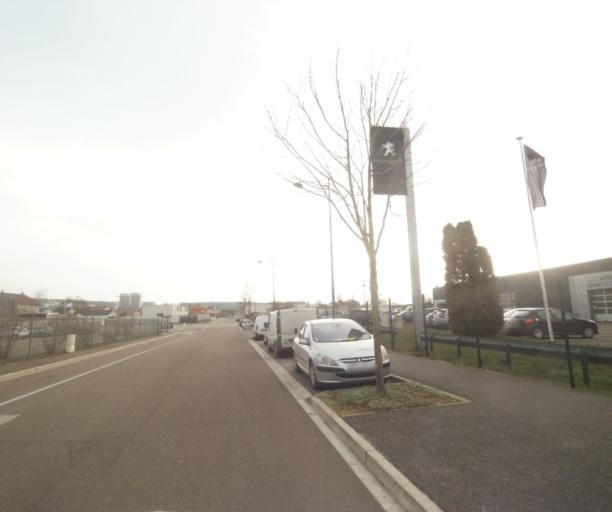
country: FR
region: Champagne-Ardenne
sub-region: Departement de la Haute-Marne
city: Bettancourt-la-Ferree
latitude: 48.6381
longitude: 4.9659
